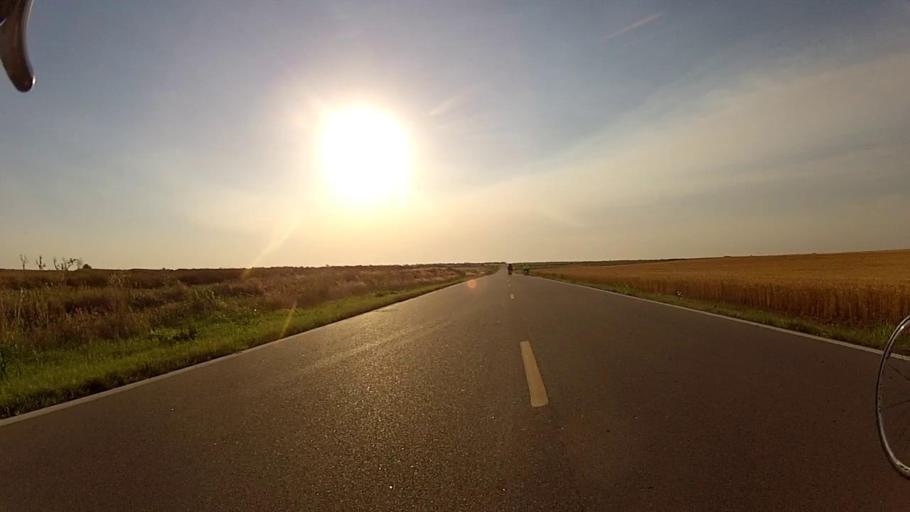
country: US
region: Kansas
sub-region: Harper County
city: Anthony
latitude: 37.1546
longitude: -97.8139
